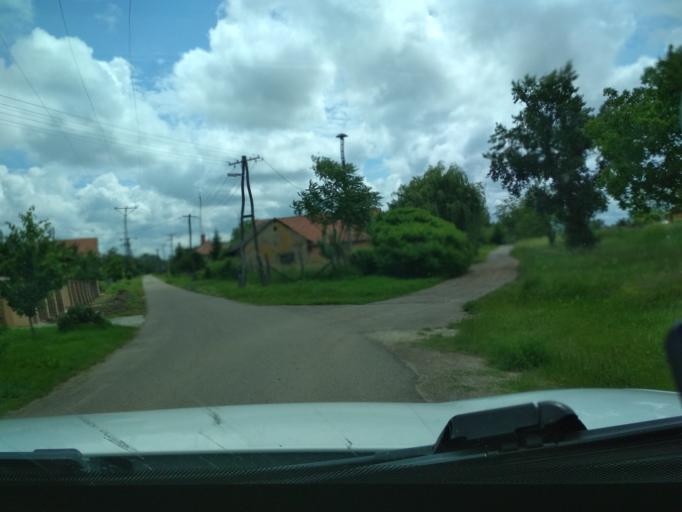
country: HU
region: Jasz-Nagykun-Szolnok
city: Tiszafured
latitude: 47.6065
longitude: 20.7243
